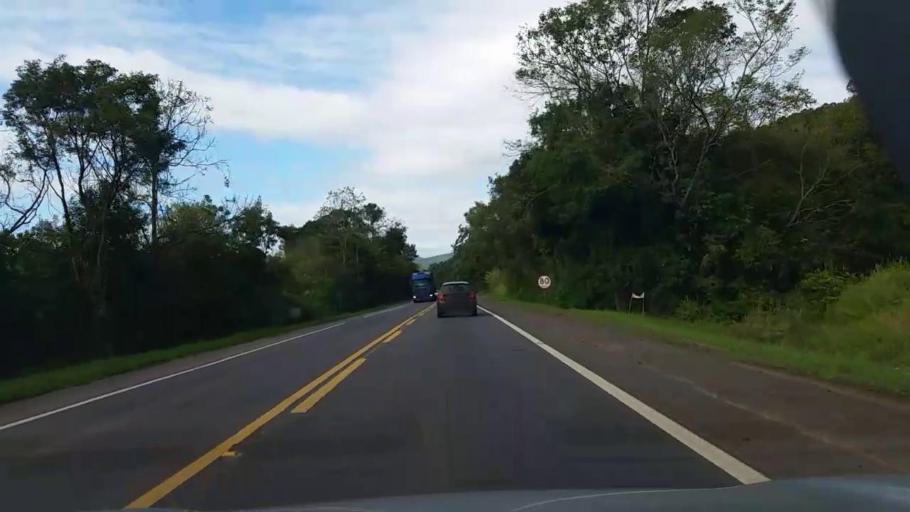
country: BR
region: Rio Grande do Sul
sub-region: Arroio Do Meio
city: Arroio do Meio
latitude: -29.3356
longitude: -52.0883
